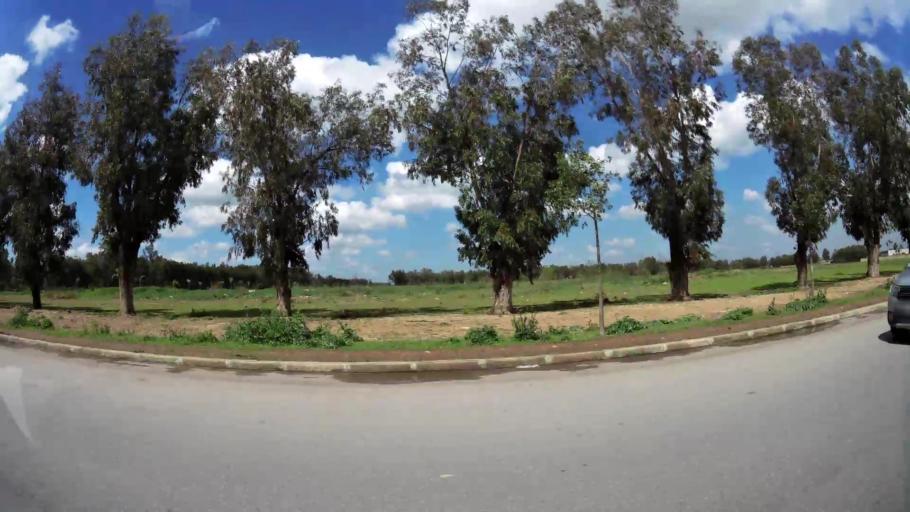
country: MA
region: Chaouia-Ouardigha
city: Nouaseur
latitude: 33.3738
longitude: -7.5536
